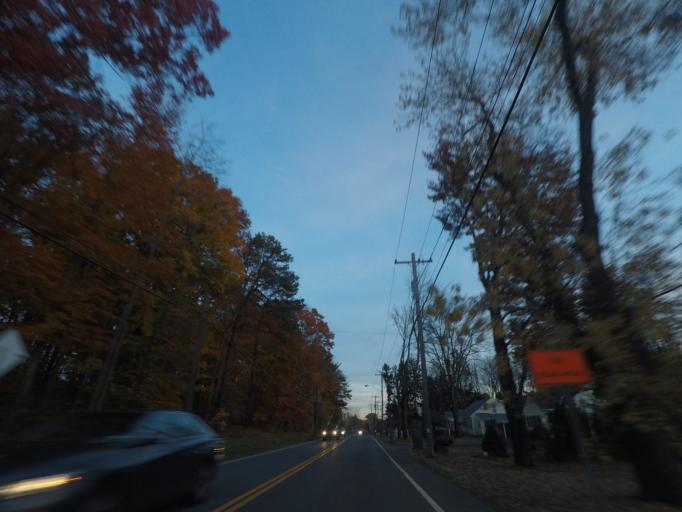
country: US
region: New York
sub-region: Schenectady County
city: Rotterdam
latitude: 42.7637
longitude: -73.9371
